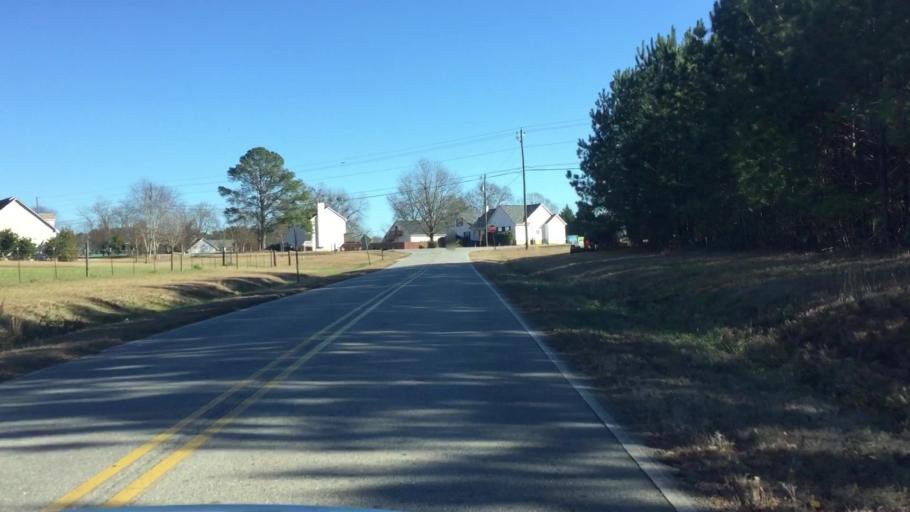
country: US
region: Georgia
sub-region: Newton County
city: Oakwood
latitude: 33.4677
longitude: -84.0114
